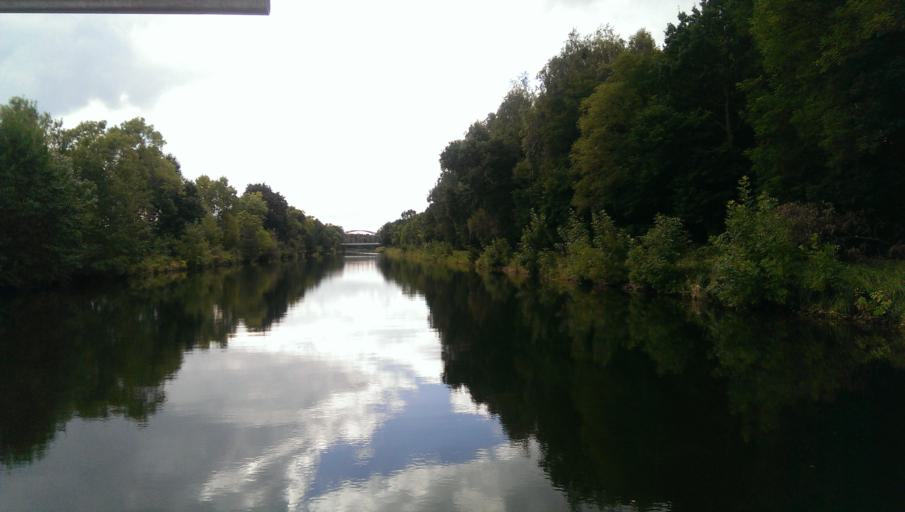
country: DE
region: Brandenburg
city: Marienwerder
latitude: 52.8472
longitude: 13.5531
